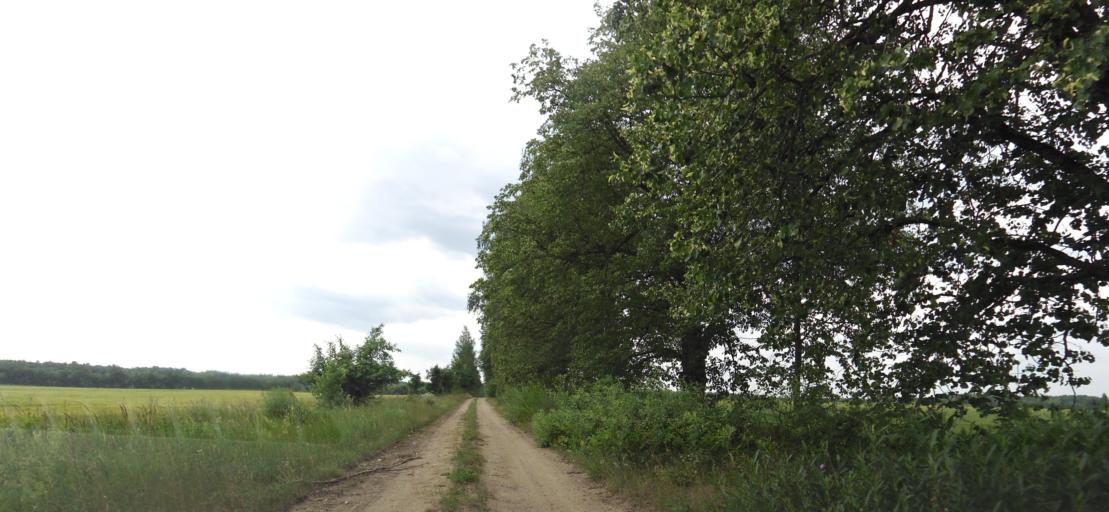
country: LT
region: Panevezys
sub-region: Birzai
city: Birzai
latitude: 56.3601
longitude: 24.9581
